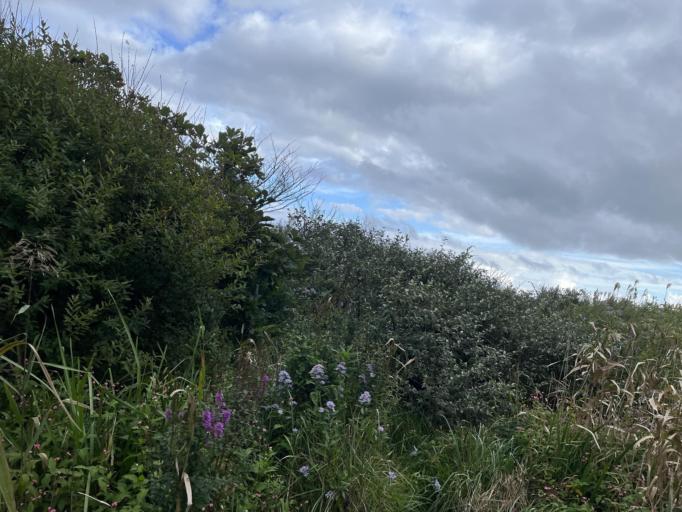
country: JP
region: Hokkaido
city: Muroran
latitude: 42.3308
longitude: 141.0199
